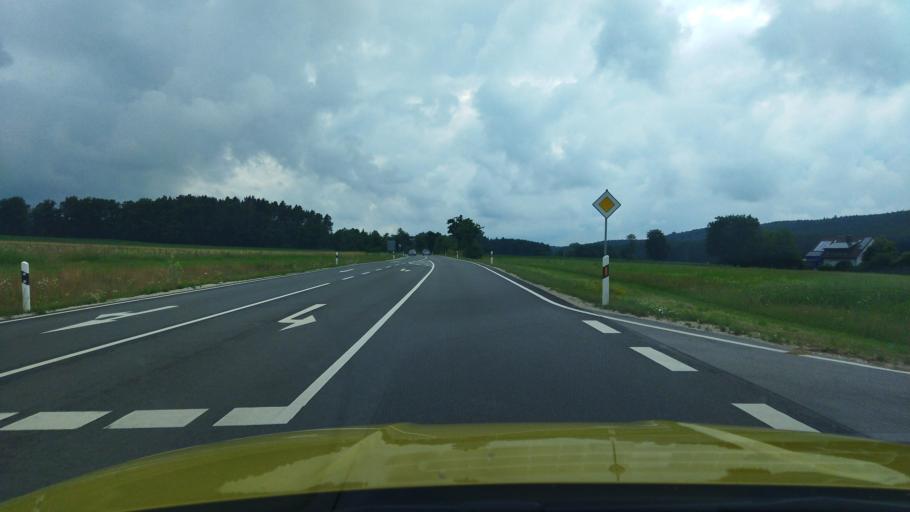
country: DE
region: Bavaria
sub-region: Regierungsbezirk Mittelfranken
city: Absberg
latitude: 49.1097
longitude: 10.9119
